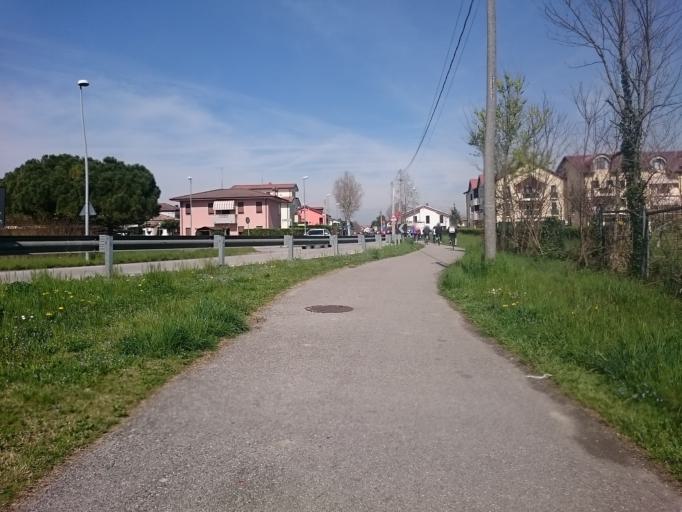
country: IT
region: Veneto
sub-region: Provincia di Padova
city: Villaguattera
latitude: 45.4378
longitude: 11.8364
